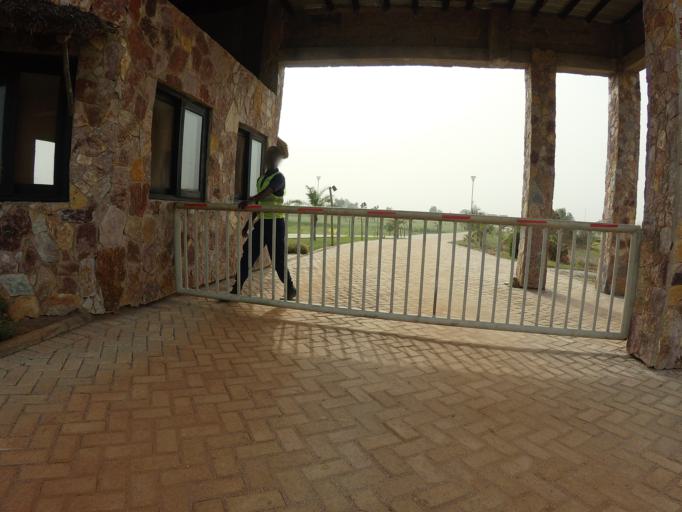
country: GH
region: Volta
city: Anloga
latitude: 5.9664
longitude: 0.6210
